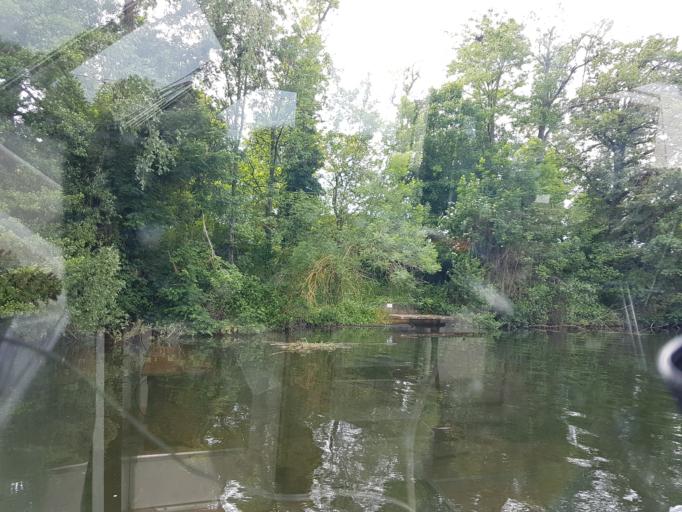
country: FR
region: Bourgogne
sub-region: Departement de l'Yonne
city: Gurgy
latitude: 47.8530
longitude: 3.5578
